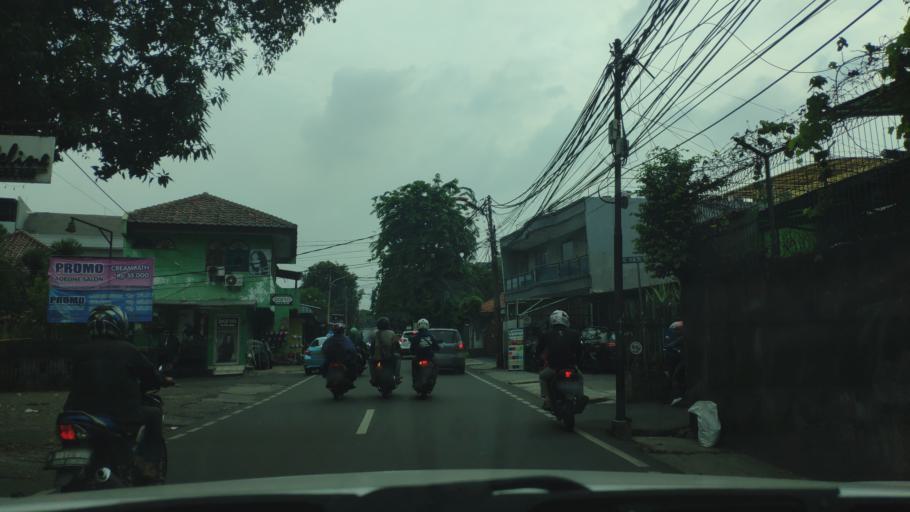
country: ID
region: Jakarta Raya
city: Jakarta
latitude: -6.1894
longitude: 106.7864
